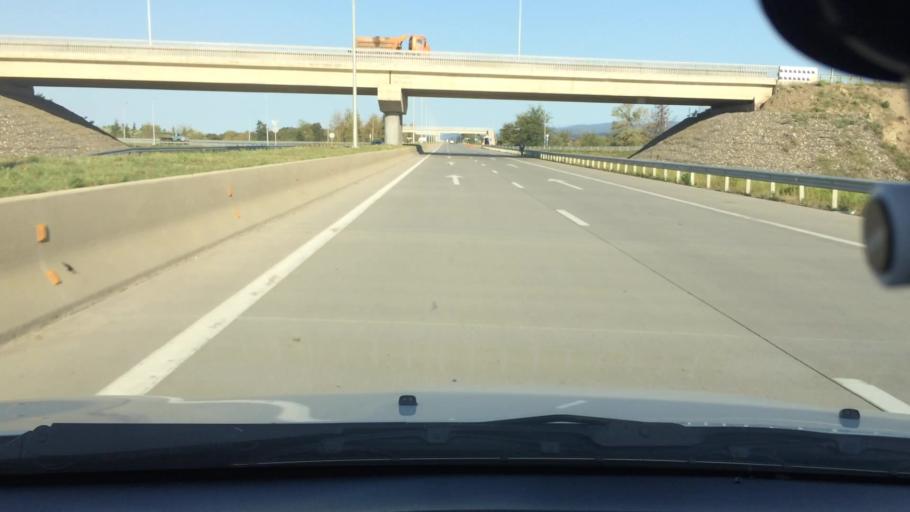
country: GE
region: Imereti
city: Zestap'oni
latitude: 42.1585
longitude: 42.9509
